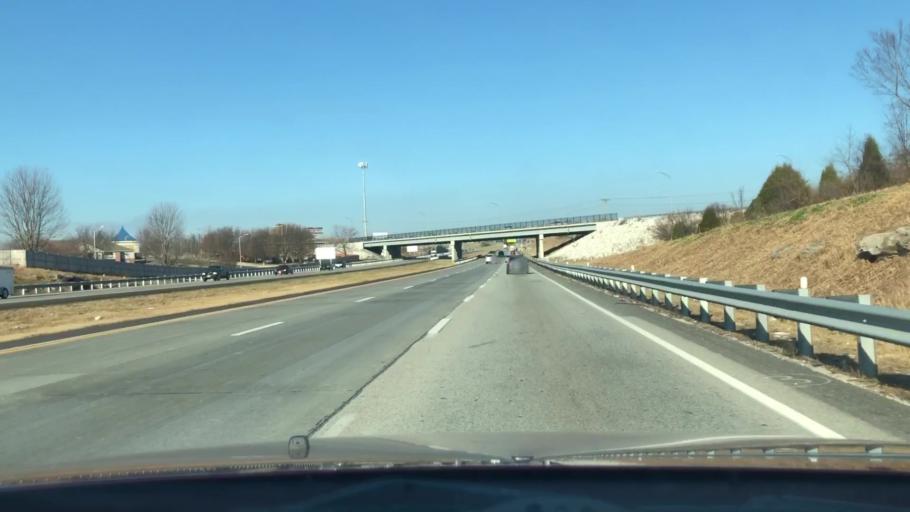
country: US
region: Missouri
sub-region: Greene County
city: Battlefield
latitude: 37.1369
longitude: -93.3083
